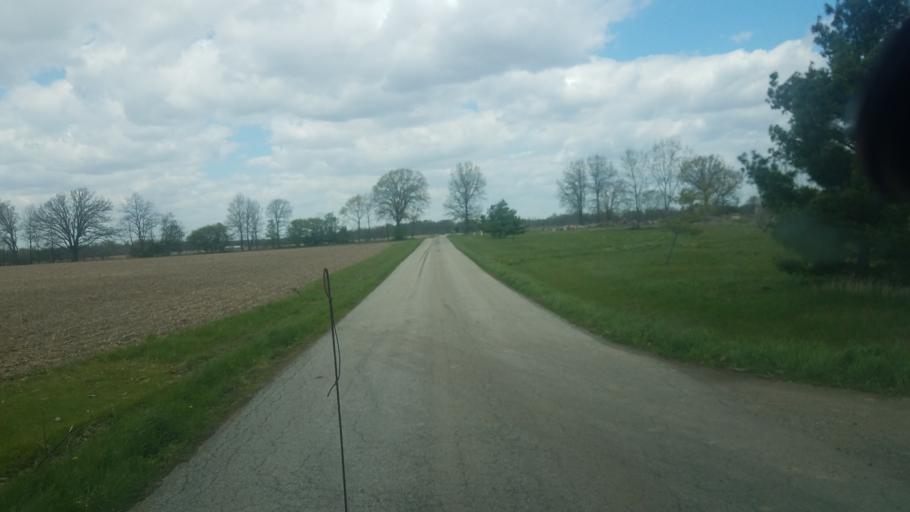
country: US
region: Ohio
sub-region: Crawford County
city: Galion
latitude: 40.7250
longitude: -82.8347
